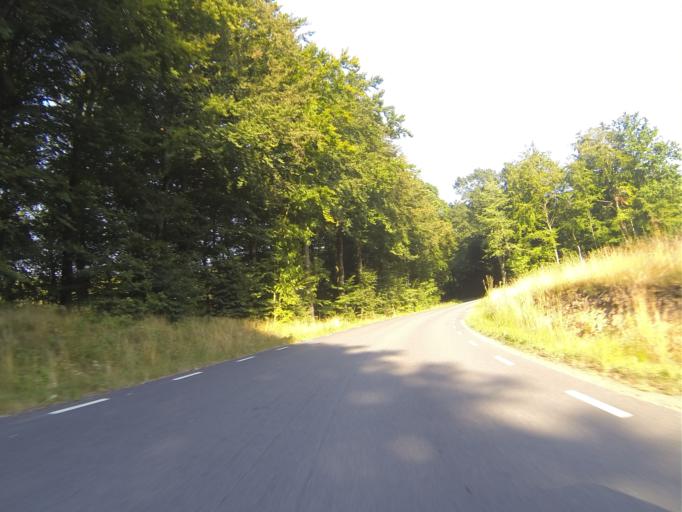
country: SE
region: Skane
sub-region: Lunds Kommun
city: Genarp
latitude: 55.5908
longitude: 13.3573
